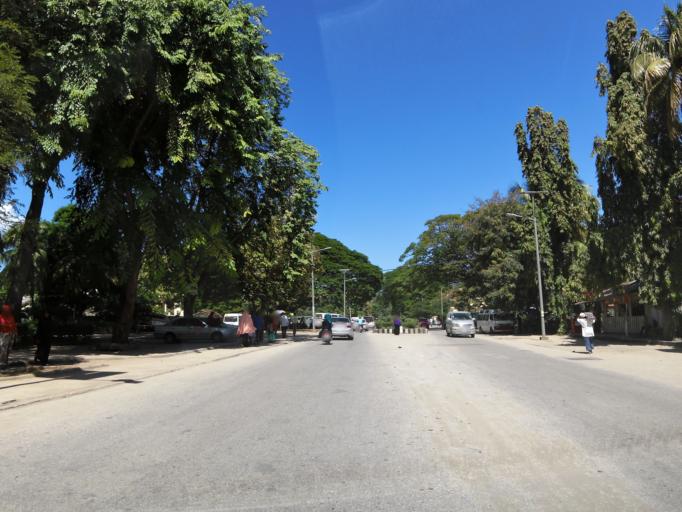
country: TZ
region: Zanzibar Urban/West
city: Zanzibar
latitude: -6.1652
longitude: 39.1927
